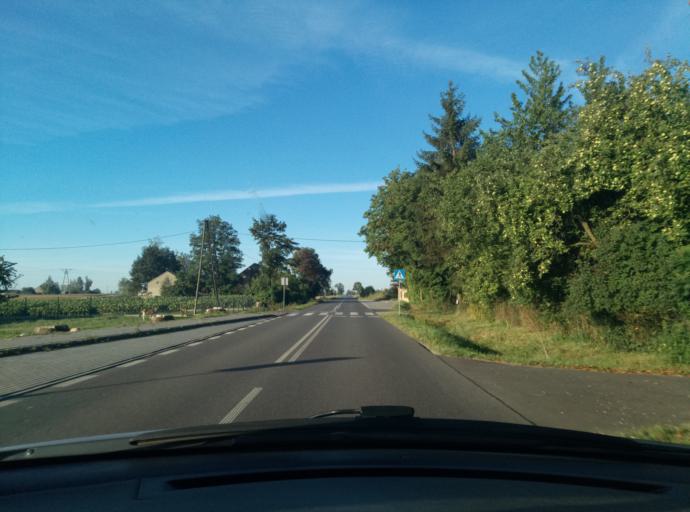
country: PL
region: Kujawsko-Pomorskie
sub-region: Powiat golubsko-dobrzynski
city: Kowalewo Pomorskie
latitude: 53.1888
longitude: 18.9101
